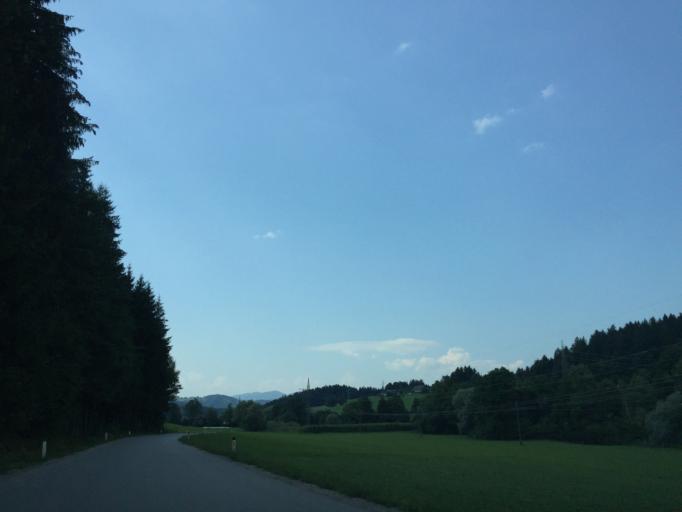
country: SI
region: Slovenj Gradec
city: Smartno pri Slovenj Gradcu
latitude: 46.4586
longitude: 15.1013
